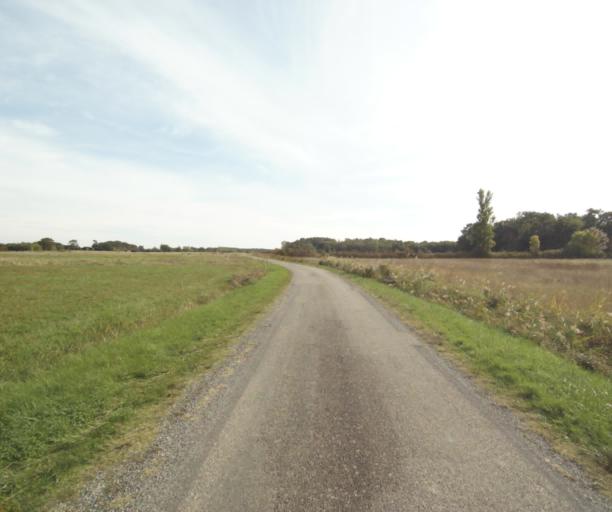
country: FR
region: Midi-Pyrenees
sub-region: Departement du Tarn-et-Garonne
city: Labastide-Saint-Pierre
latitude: 43.9000
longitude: 1.3852
